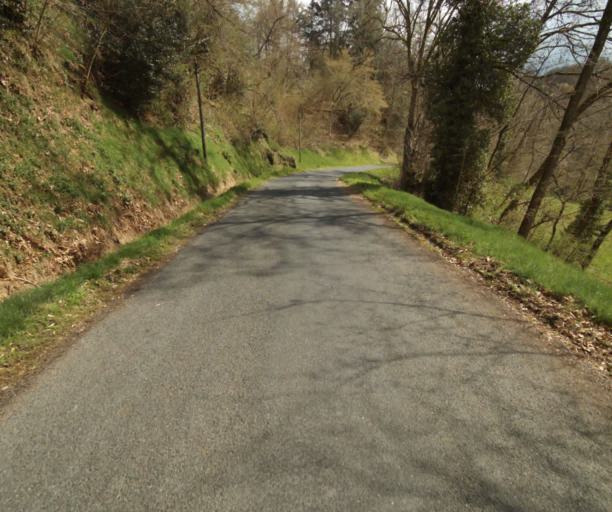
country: FR
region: Limousin
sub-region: Departement de la Correze
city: Laguenne
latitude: 45.2518
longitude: 1.8861
